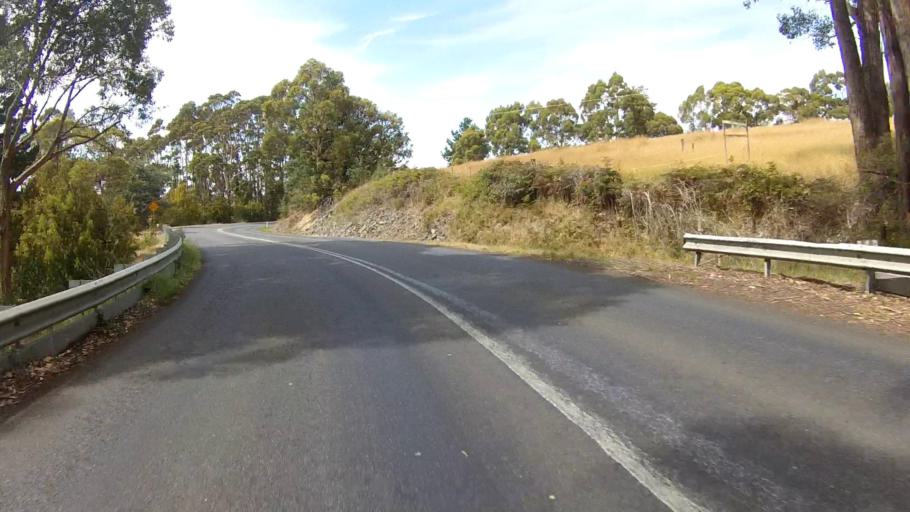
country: AU
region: Tasmania
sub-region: Kingborough
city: Kettering
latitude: -43.1443
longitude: 147.2425
